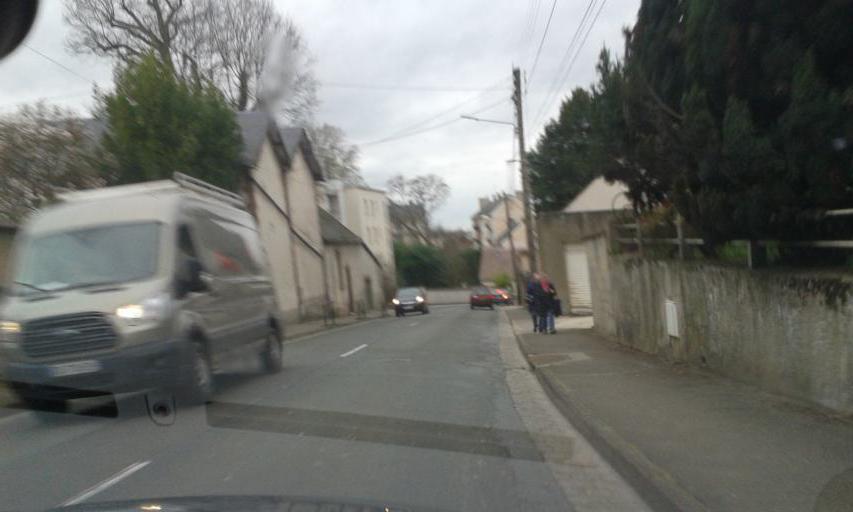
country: FR
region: Centre
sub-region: Departement d'Eure-et-Loir
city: Chartres
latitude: 48.4407
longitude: 1.5012
